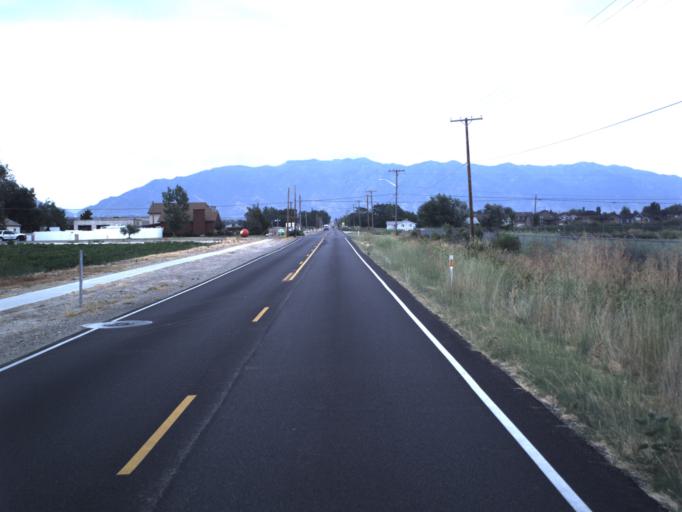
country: US
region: Utah
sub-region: Davis County
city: West Point
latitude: 41.0892
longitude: -112.1048
